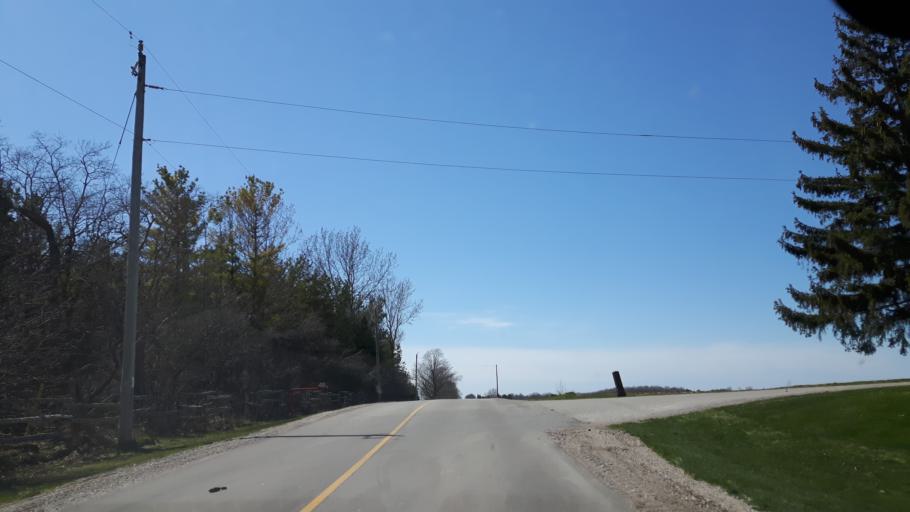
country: CA
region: Ontario
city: Bluewater
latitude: 43.5799
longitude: -81.6538
